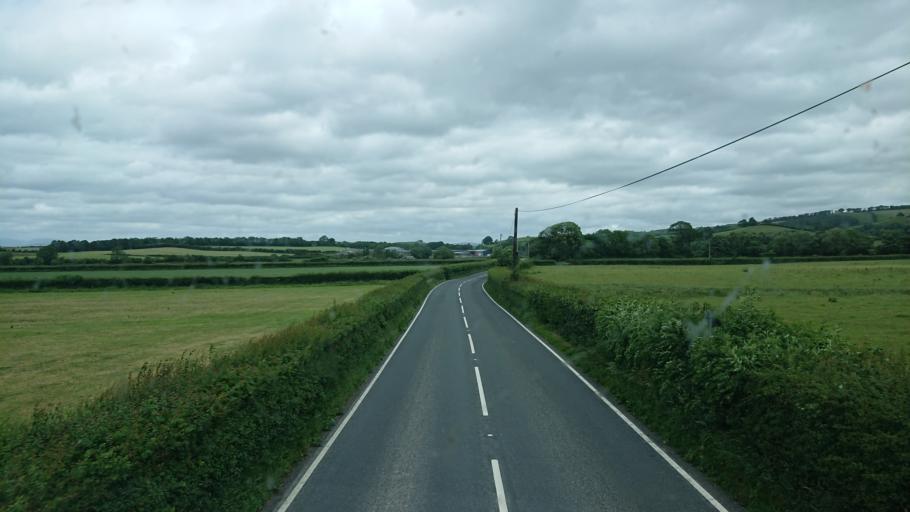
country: GB
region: England
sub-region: Cumbria
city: Milnthorpe
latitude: 54.2270
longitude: -2.7159
